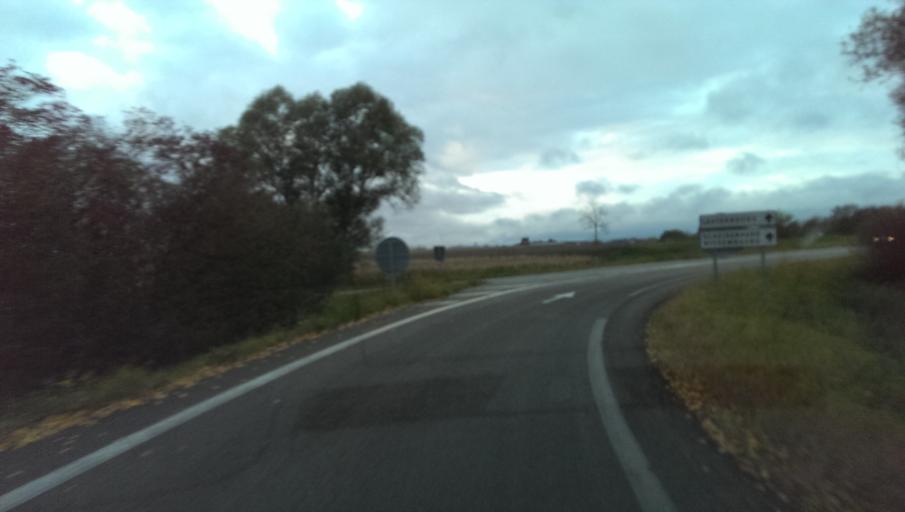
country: DE
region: Rheinland-Pfalz
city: Scheibenhardt
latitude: 48.9726
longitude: 8.1520
